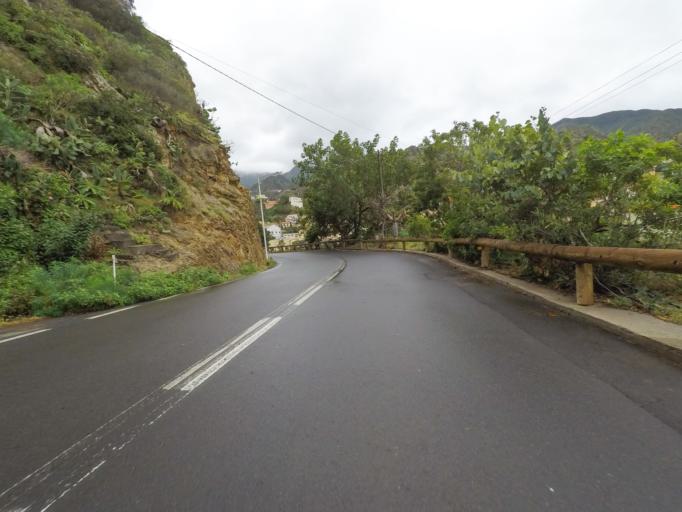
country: ES
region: Canary Islands
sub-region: Provincia de Santa Cruz de Tenerife
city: Vallehermosa
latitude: 28.1805
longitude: -17.2631
